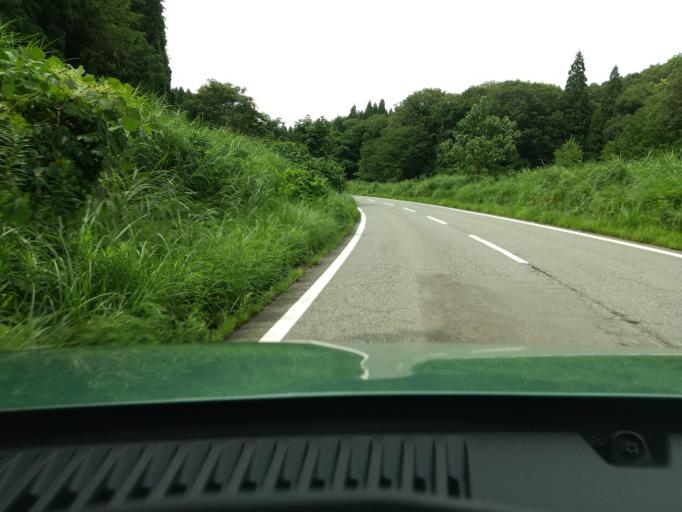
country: JP
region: Akita
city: Akita
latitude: 39.7274
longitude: 140.1835
